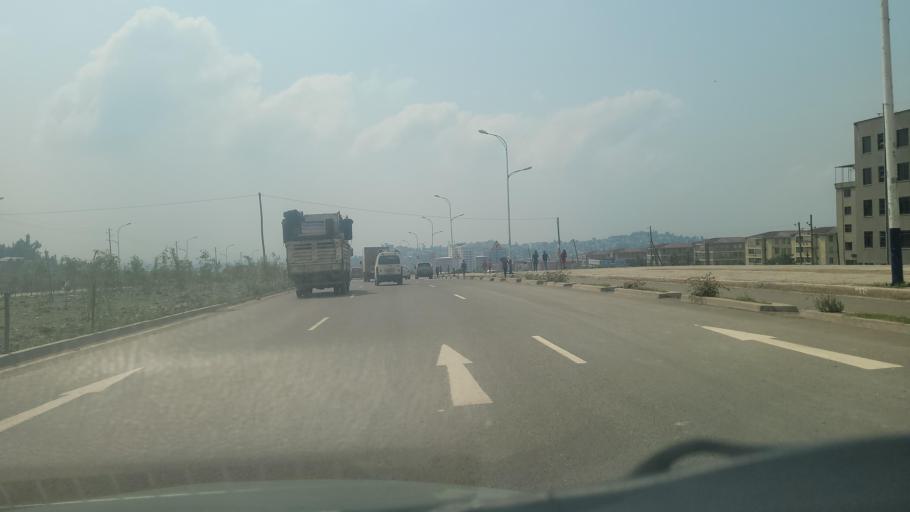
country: ET
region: Adis Abeba
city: Addis Ababa
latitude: 8.9392
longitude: 38.7255
